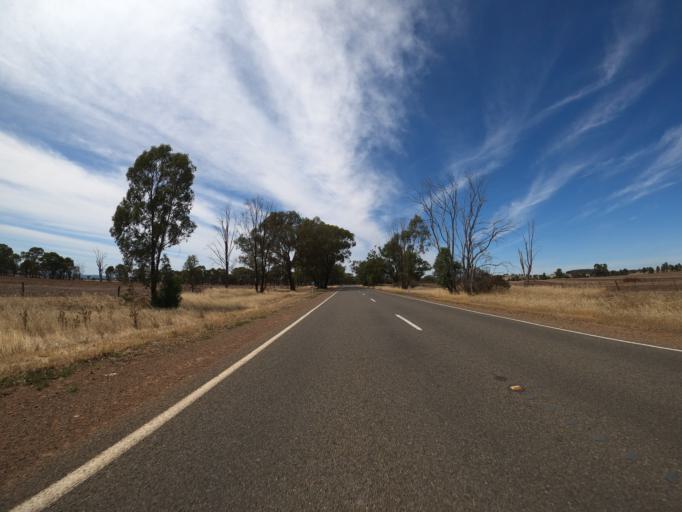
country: AU
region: Victoria
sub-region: Benalla
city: Benalla
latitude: -36.3036
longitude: 145.9559
